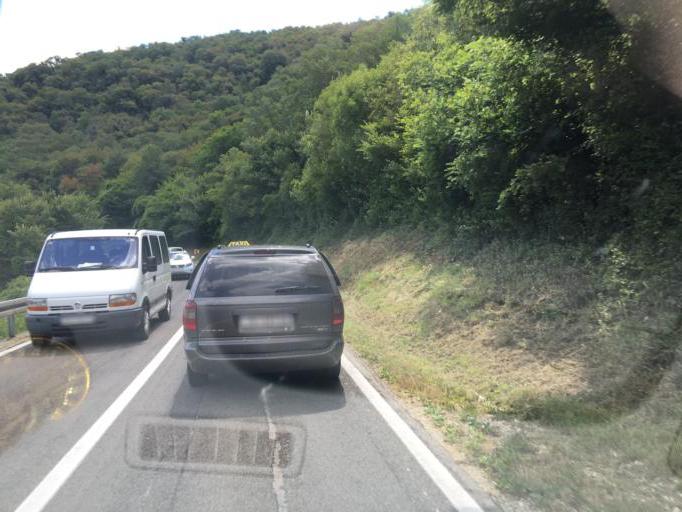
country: HR
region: Istarska
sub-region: Grad Rovinj
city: Rovinj
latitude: 45.1277
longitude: 13.7446
